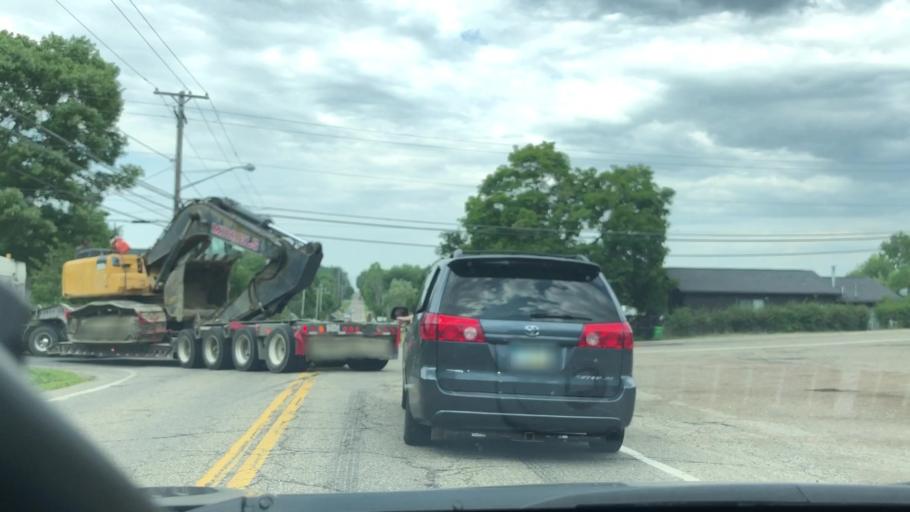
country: US
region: Ohio
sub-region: Summit County
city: New Franklin
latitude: 40.9207
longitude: -81.5358
